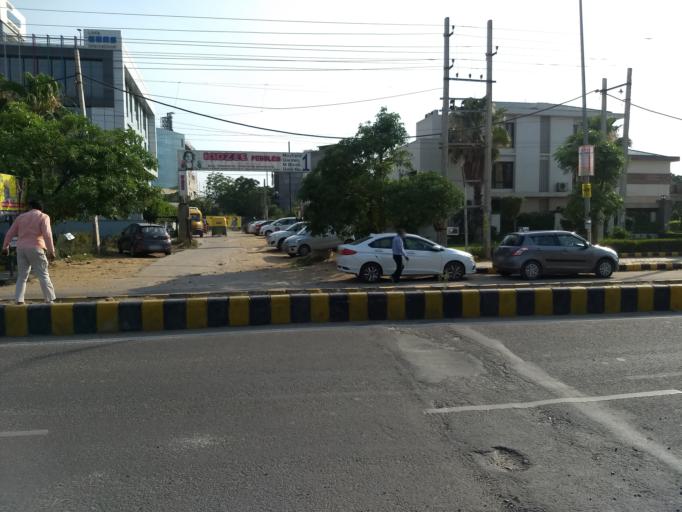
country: IN
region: Haryana
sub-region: Gurgaon
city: Gurgaon
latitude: 28.4329
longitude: 77.0724
